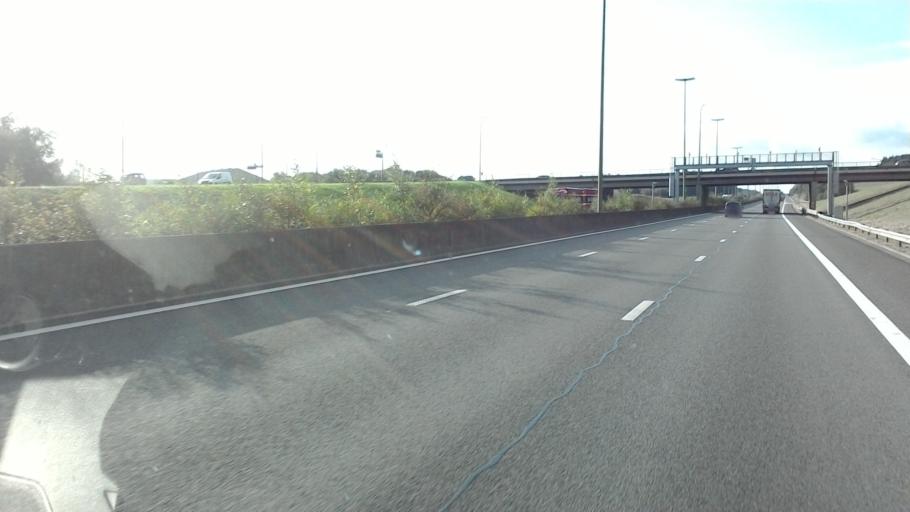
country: BE
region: Wallonia
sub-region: Province du Luxembourg
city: Habay-la-Vieille
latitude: 49.7053
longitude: 5.6272
